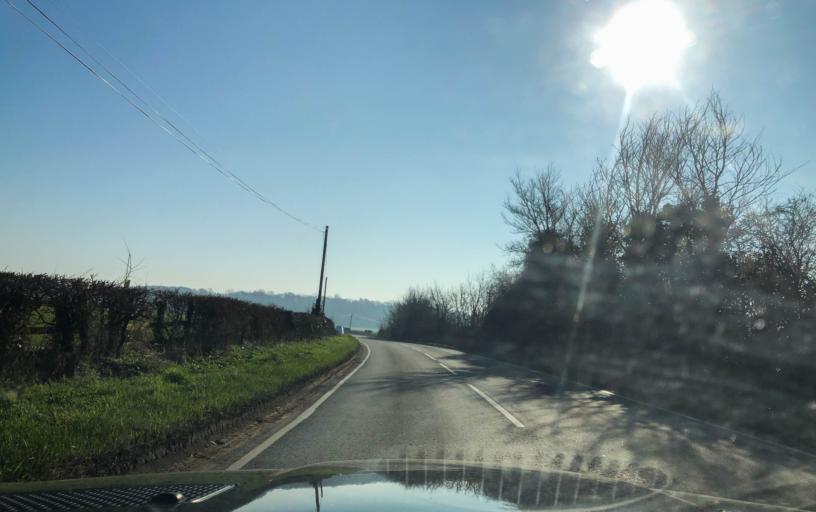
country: GB
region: England
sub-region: Warwickshire
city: Wellesbourne Mountford
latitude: 52.1879
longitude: -1.5820
